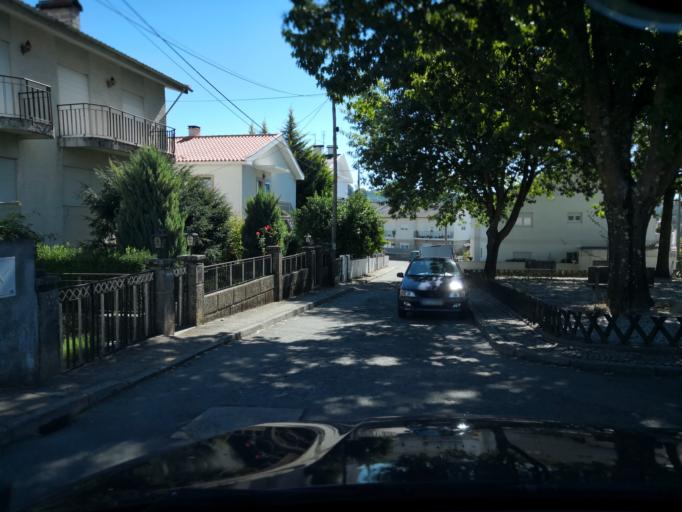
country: PT
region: Vila Real
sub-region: Vila Real
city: Vila Real
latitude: 41.2972
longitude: -7.7520
